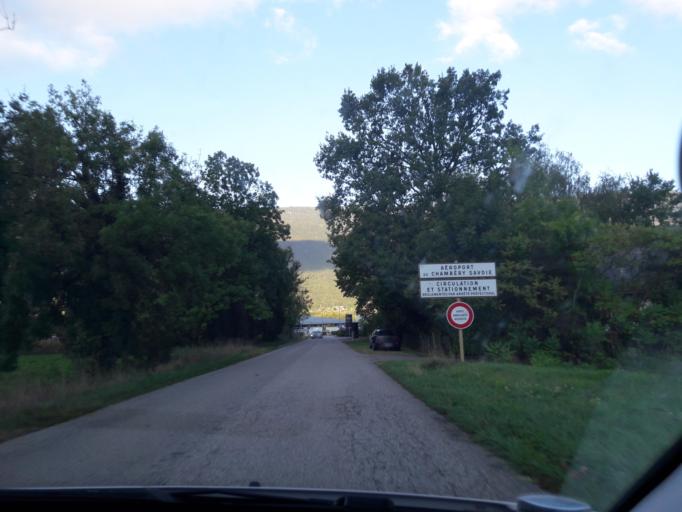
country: FR
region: Rhone-Alpes
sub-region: Departement de la Savoie
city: Voglans
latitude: 45.6382
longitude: 5.8871
